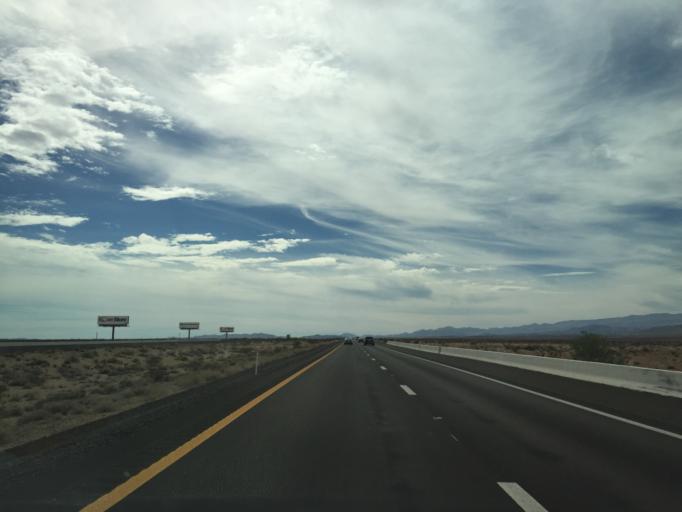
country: US
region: Nevada
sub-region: Clark County
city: Moapa Town
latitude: 36.5779
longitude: -114.6602
